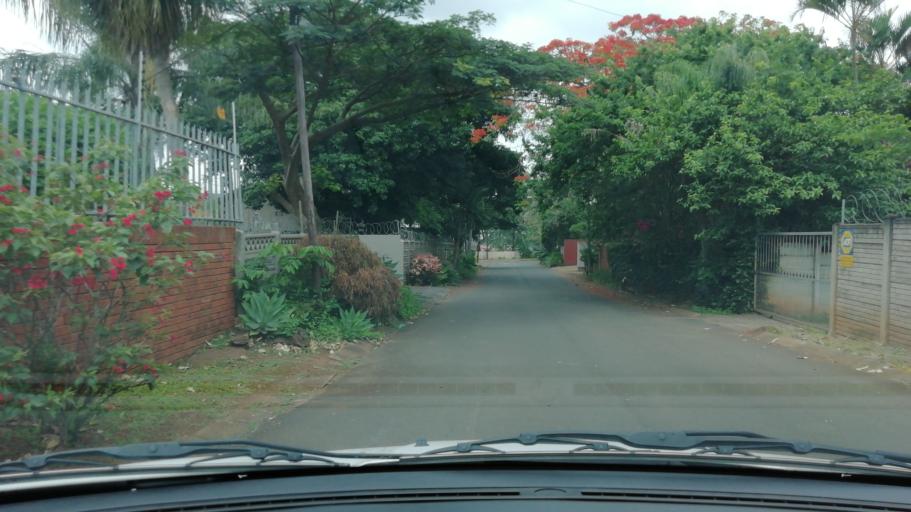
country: ZA
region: KwaZulu-Natal
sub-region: uThungulu District Municipality
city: Empangeni
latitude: -28.7500
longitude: 31.8935
